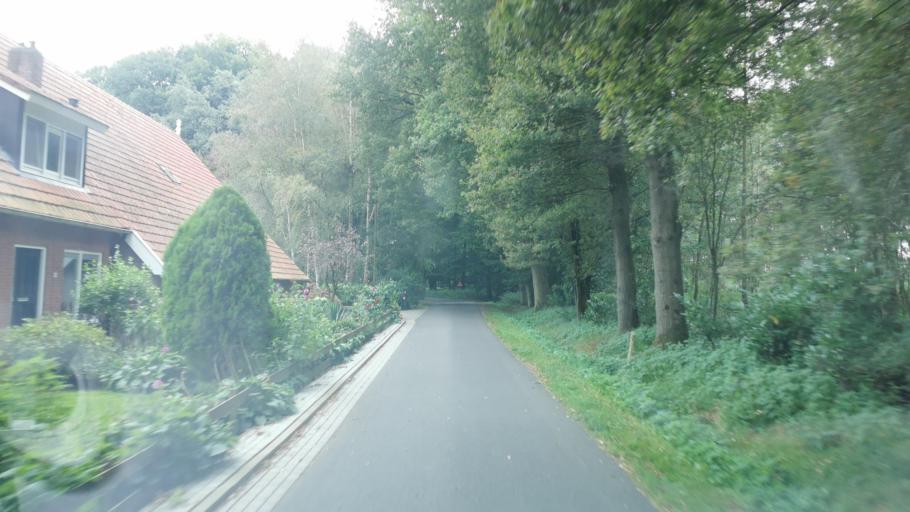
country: NL
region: Overijssel
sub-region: Gemeente Oldenzaal
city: Oldenzaal
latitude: 52.3021
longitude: 6.9685
